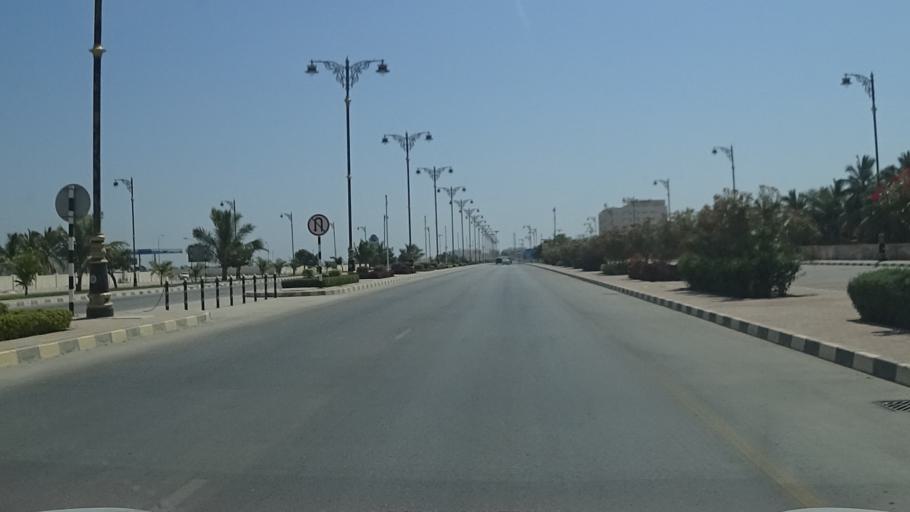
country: OM
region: Zufar
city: Salalah
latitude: 17.0312
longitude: 54.1722
